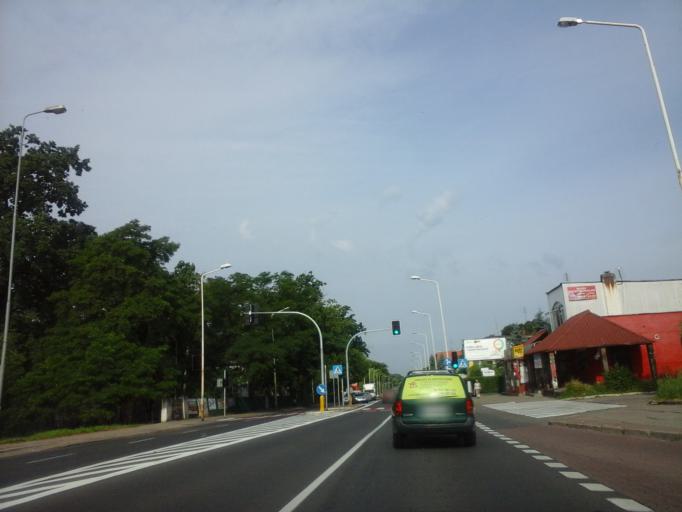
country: PL
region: West Pomeranian Voivodeship
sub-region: Powiat stargardzki
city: Stargard Szczecinski
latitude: 53.3390
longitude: 15.0278
